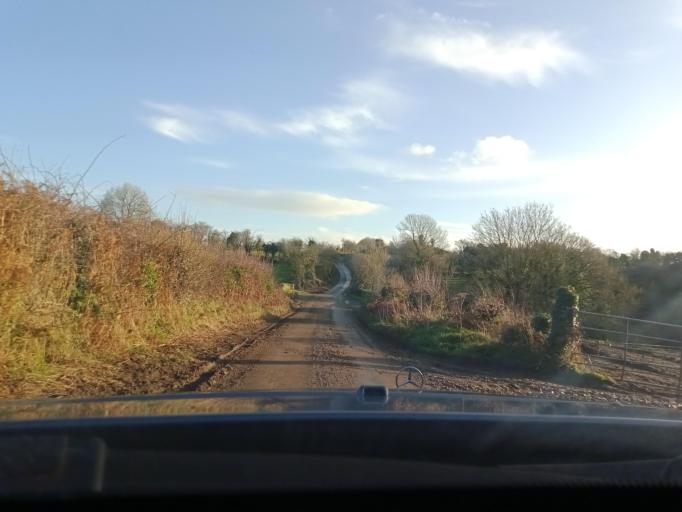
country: IE
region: Munster
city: Carrick-on-Suir
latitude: 52.4387
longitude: -7.4015
